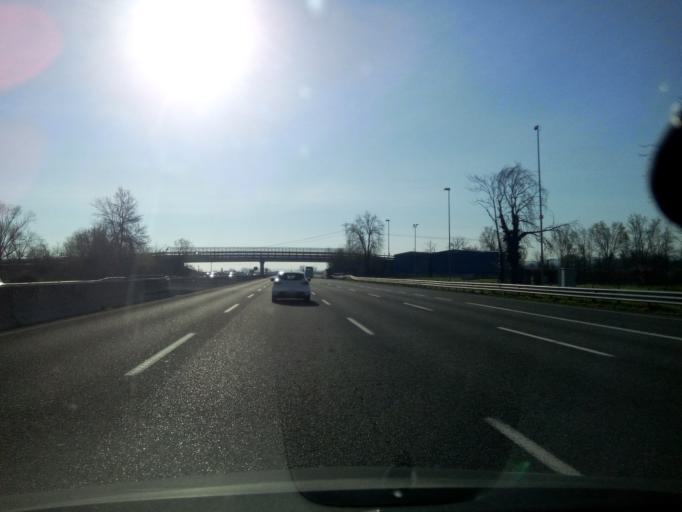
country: IT
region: Emilia-Romagna
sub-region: Provincia di Modena
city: Piumazzo
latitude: 44.5586
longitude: 11.0601
